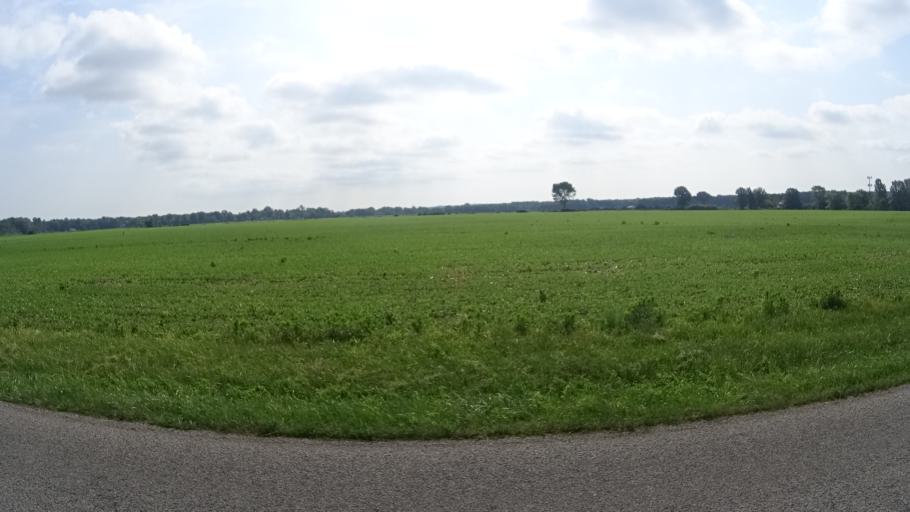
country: US
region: Ohio
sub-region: Lorain County
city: Vermilion
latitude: 41.3869
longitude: -82.4303
